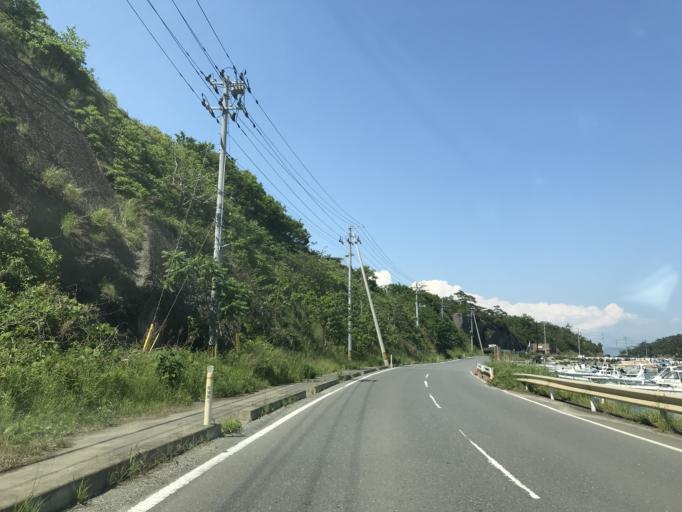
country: JP
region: Miyagi
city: Matsushima
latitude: 38.3496
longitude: 141.1544
